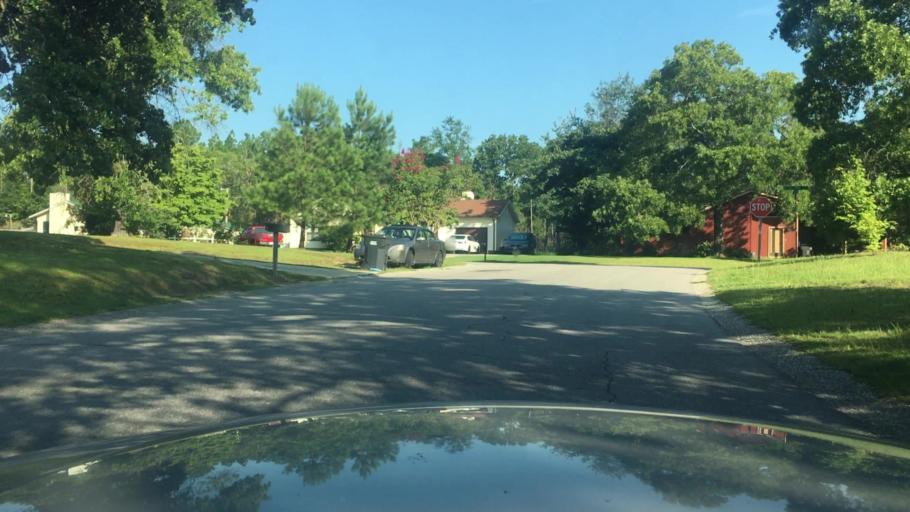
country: US
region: North Carolina
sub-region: Cumberland County
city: Spring Lake
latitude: 35.1599
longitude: -78.9088
